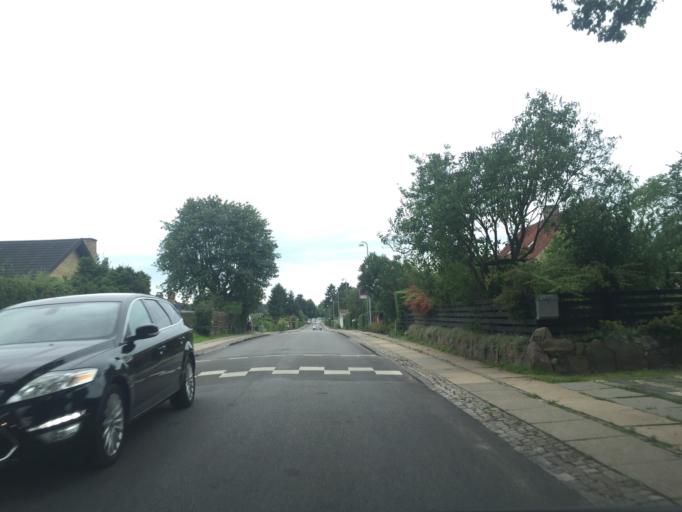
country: DK
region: Capital Region
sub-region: Lyngby-Tarbaek Kommune
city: Kongens Lyngby
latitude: 55.7906
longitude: 12.5418
